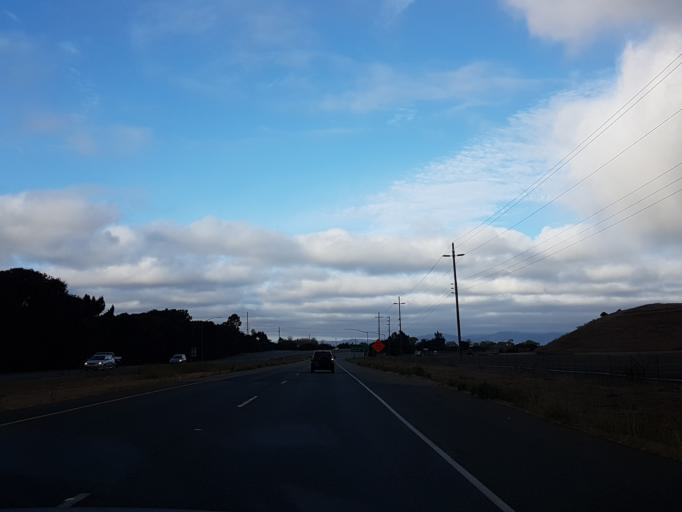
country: US
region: California
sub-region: Monterey County
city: Salinas
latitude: 36.6199
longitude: -121.6857
